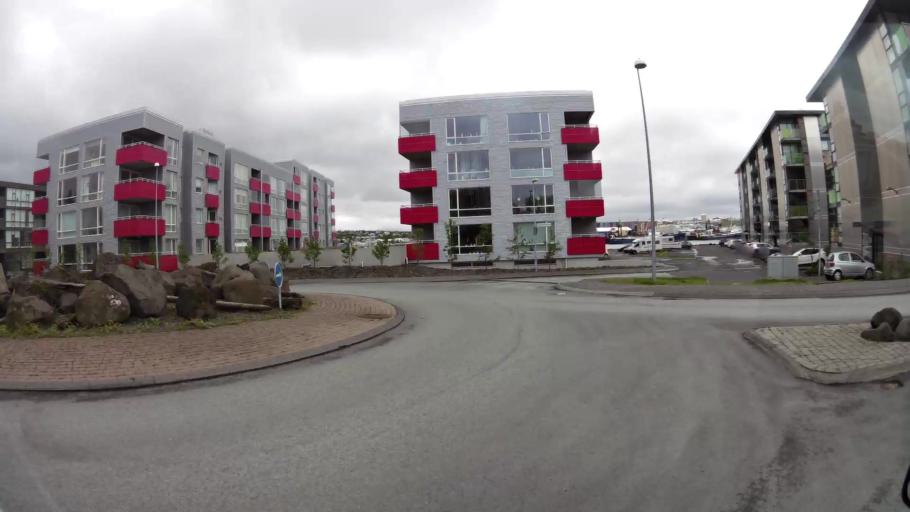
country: IS
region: Capital Region
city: Hafnarfjoerdur
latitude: 64.0700
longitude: -21.9641
